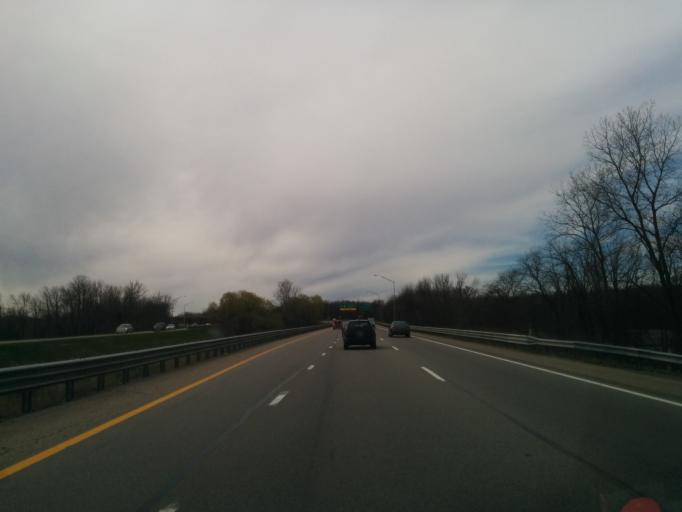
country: US
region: Michigan
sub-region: Kent County
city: Grandville
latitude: 42.9211
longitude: -85.7580
